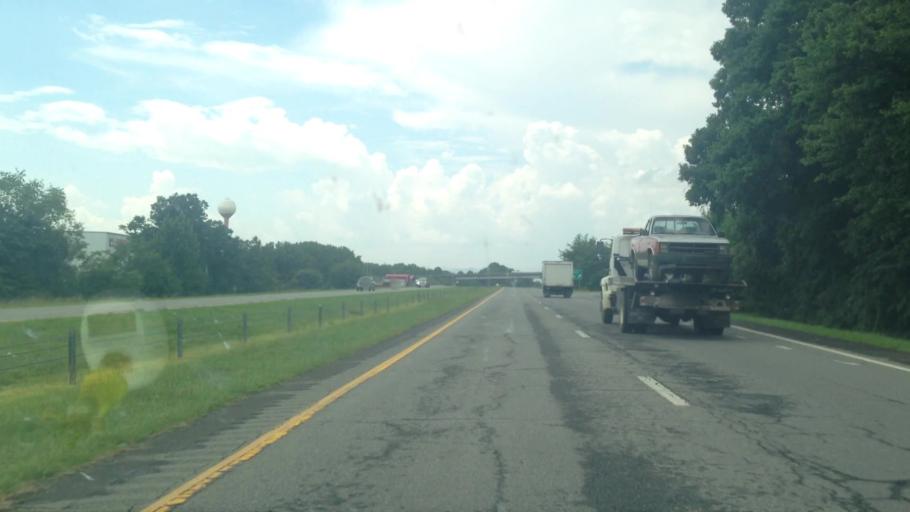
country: US
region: North Carolina
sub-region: Surry County
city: Flat Rock
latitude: 36.4572
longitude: -80.5580
